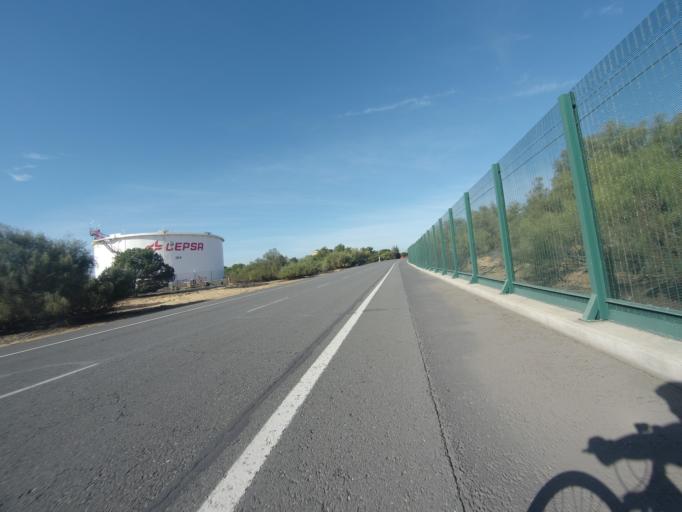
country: ES
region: Andalusia
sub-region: Provincia de Huelva
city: Punta Umbria
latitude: 37.2022
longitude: -6.9349
